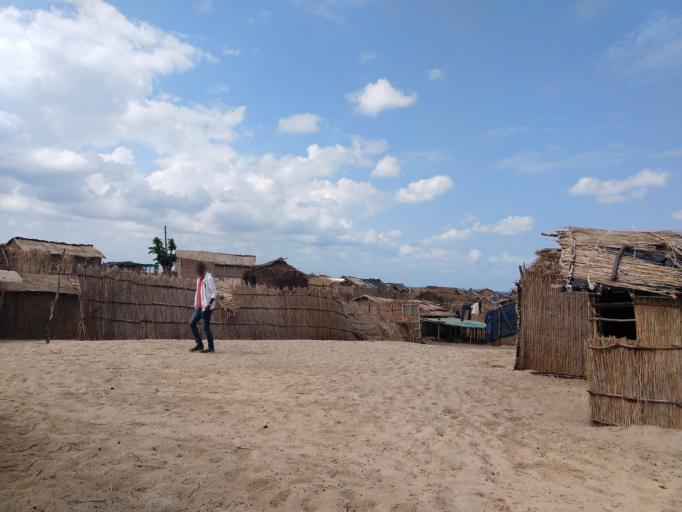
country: MZ
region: Sofala
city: Beira
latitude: -19.6489
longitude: 35.1773
